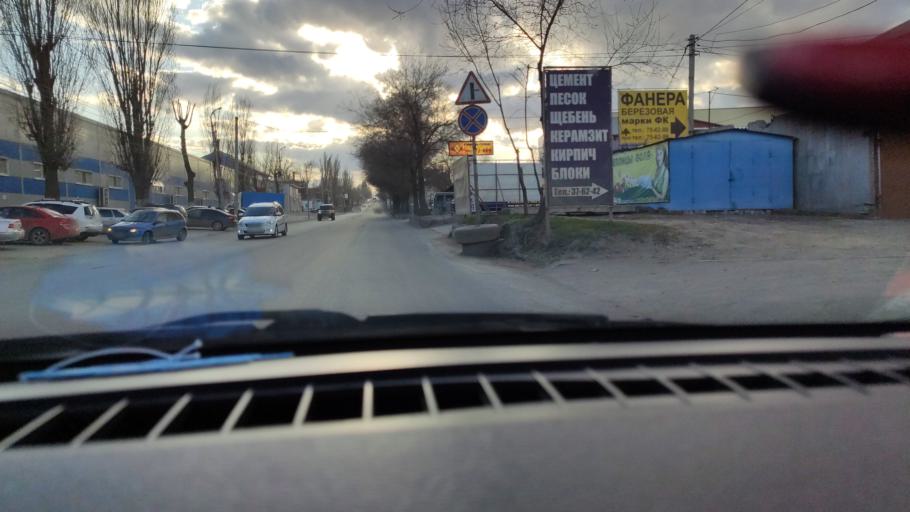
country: RU
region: Saratov
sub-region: Saratovskiy Rayon
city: Saratov
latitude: 51.6151
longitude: 45.9612
